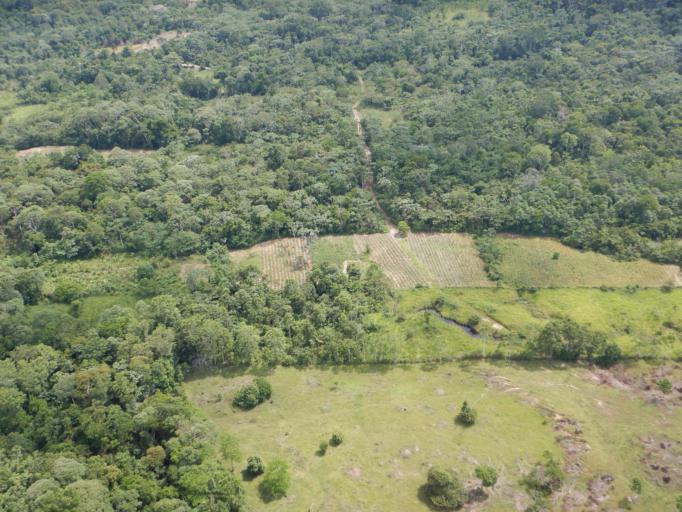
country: BO
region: Cochabamba
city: Chimore
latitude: -17.0583
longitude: -64.6156
